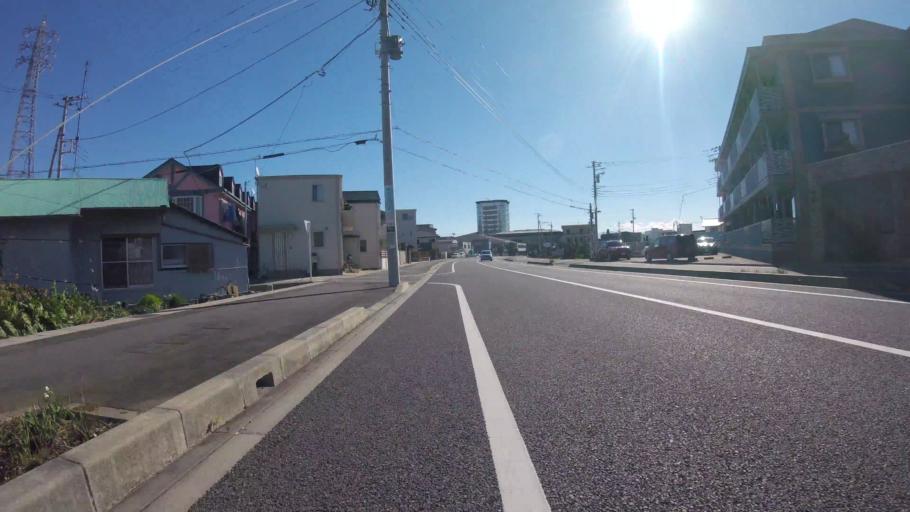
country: JP
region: Shizuoka
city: Mishima
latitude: 35.1377
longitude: 138.9098
